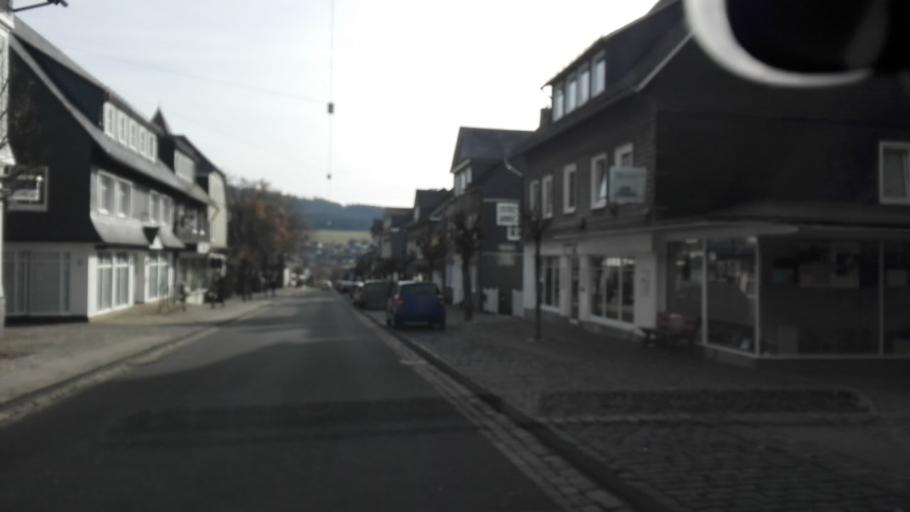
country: DE
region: North Rhine-Westphalia
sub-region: Regierungsbezirk Arnsberg
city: Schmallenberg
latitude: 51.1484
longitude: 8.2842
